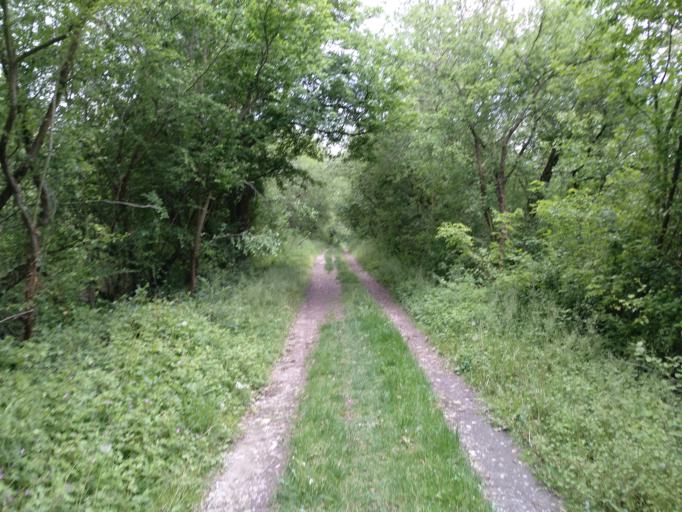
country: FR
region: Rhone-Alpes
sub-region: Departement du Rhone
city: Serezin-du-Rhone
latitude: 45.6320
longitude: 4.8131
